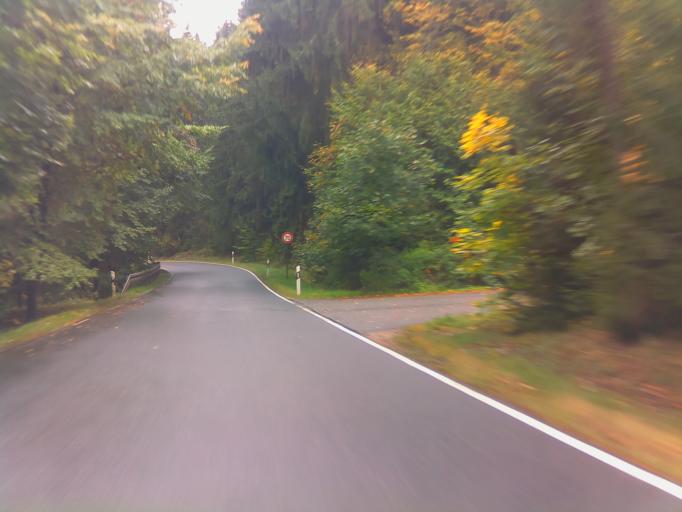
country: DE
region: Thuringia
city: Remptendorf
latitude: 50.5404
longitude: 11.6338
